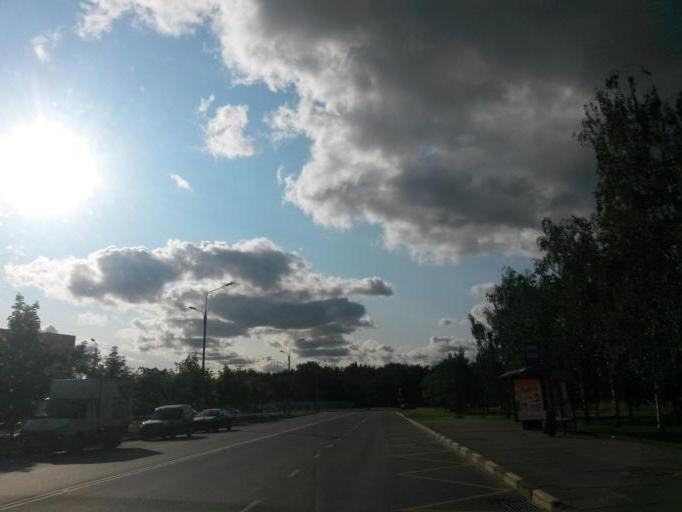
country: RU
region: Moscow
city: Zhulebino
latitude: 55.6874
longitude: 37.8490
